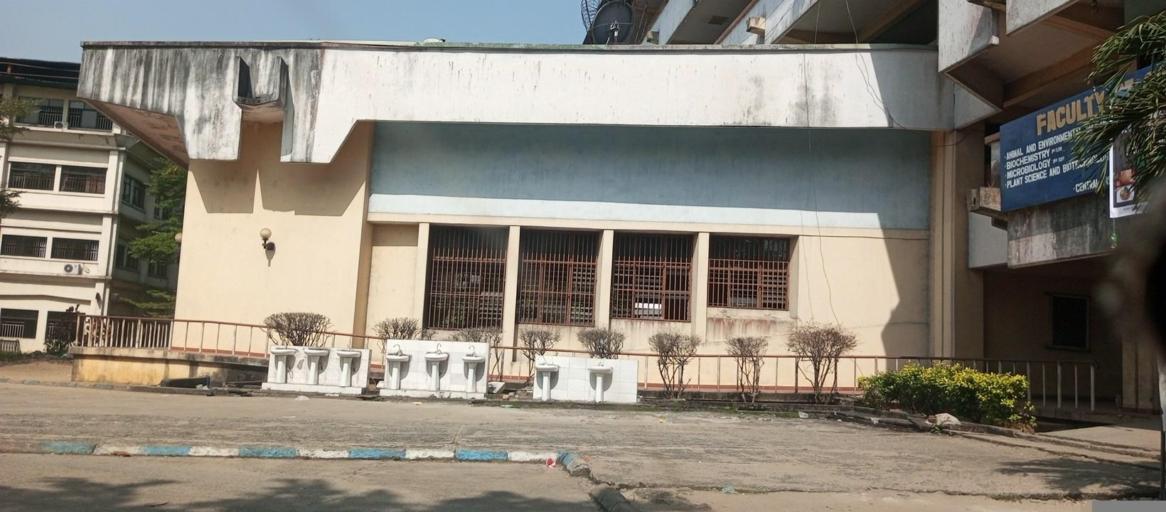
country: NG
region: Rivers
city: Emuoha
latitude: 4.9044
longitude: 6.9222
